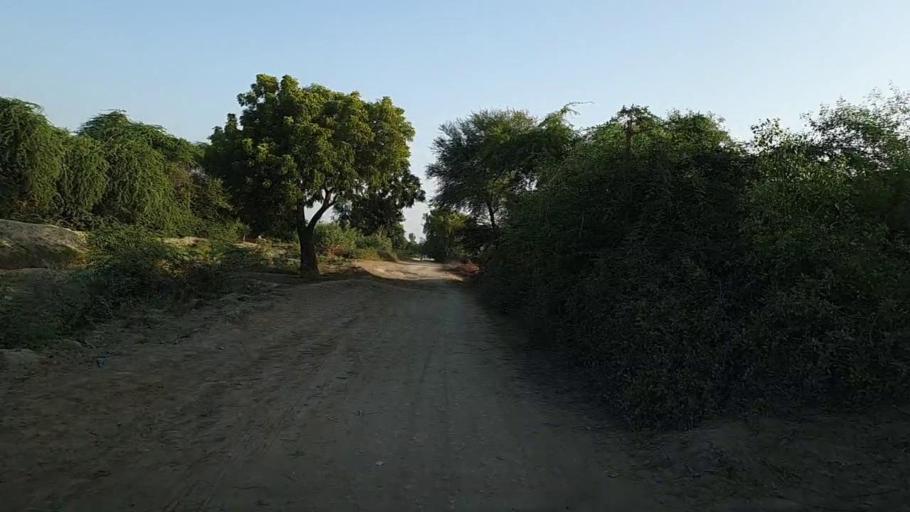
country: PK
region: Sindh
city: Kario
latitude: 24.6995
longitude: 68.6706
